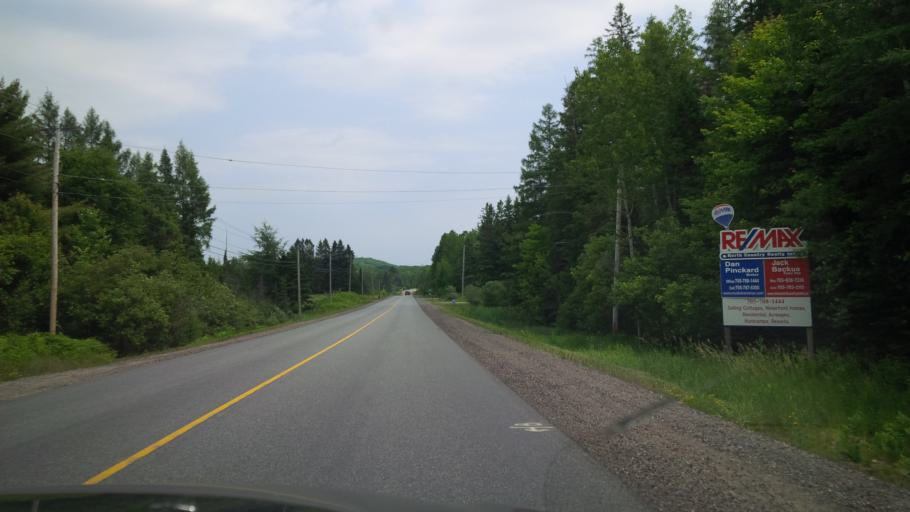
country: CA
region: Ontario
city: Huntsville
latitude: 45.5395
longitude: -79.2797
